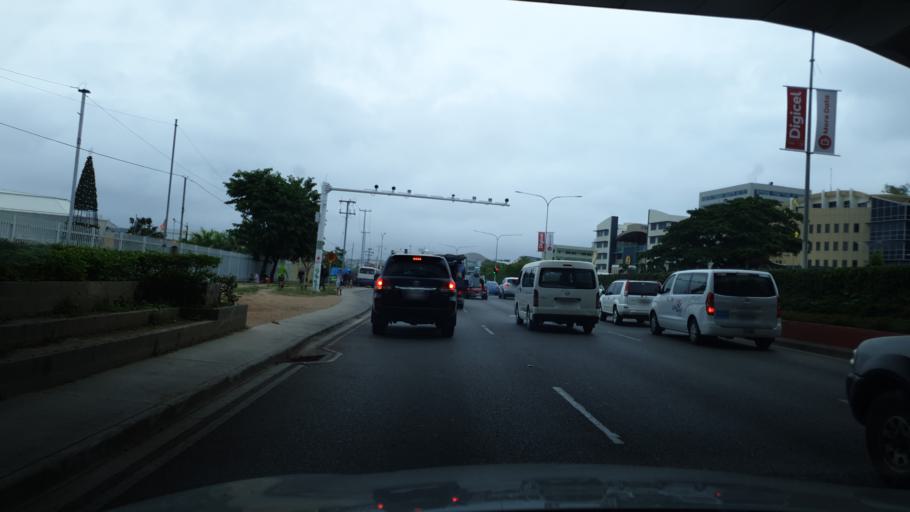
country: PG
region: National Capital
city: Port Moresby
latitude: -9.4386
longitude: 147.1803
